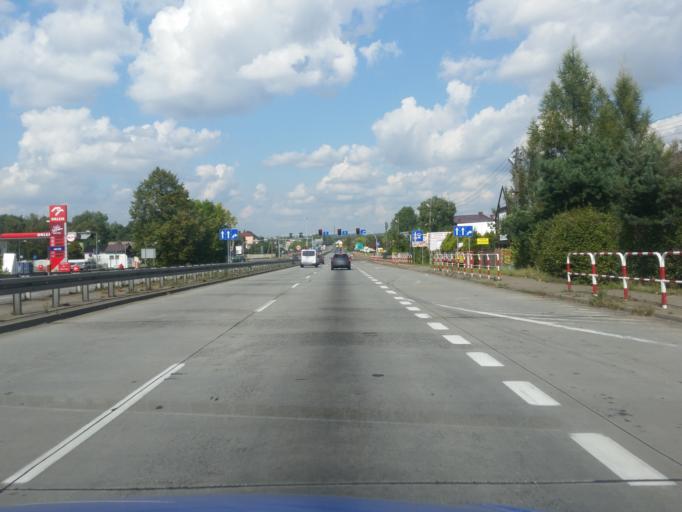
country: PL
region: Silesian Voivodeship
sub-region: Powiat bedzinski
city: Siewierz
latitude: 50.4648
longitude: 19.2307
